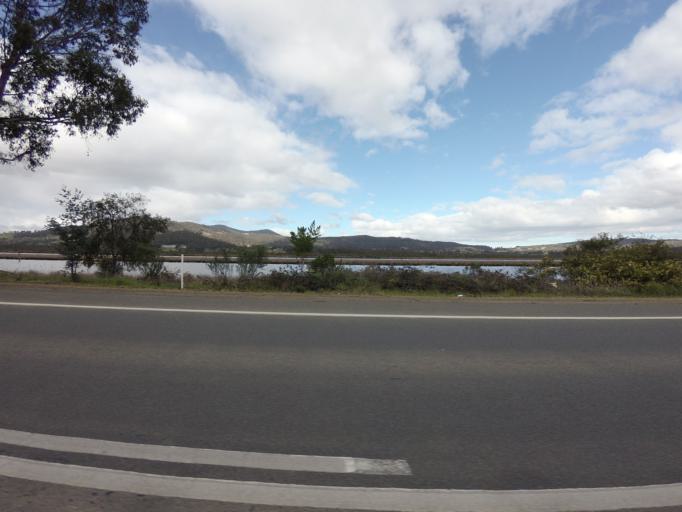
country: AU
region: Tasmania
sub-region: Huon Valley
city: Franklin
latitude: -43.0957
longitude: 147.0070
